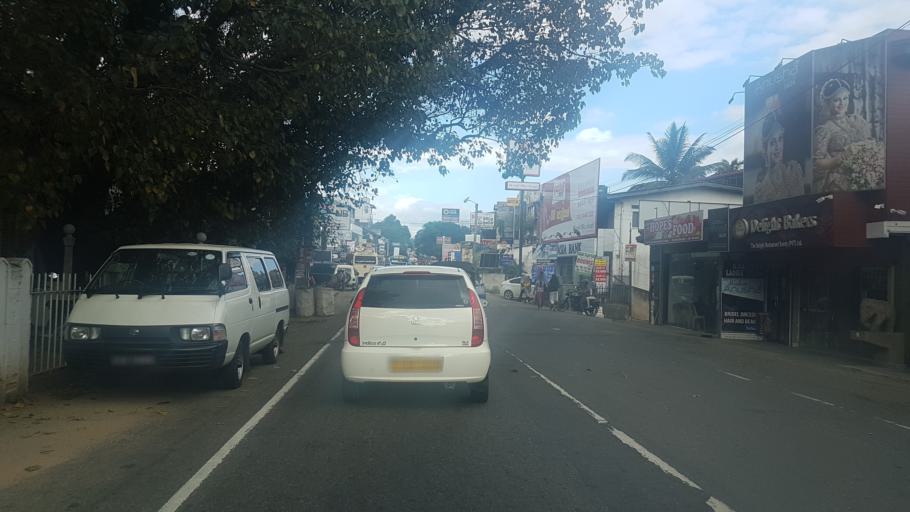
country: LK
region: Central
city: Kandy
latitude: 7.2788
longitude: 80.6175
